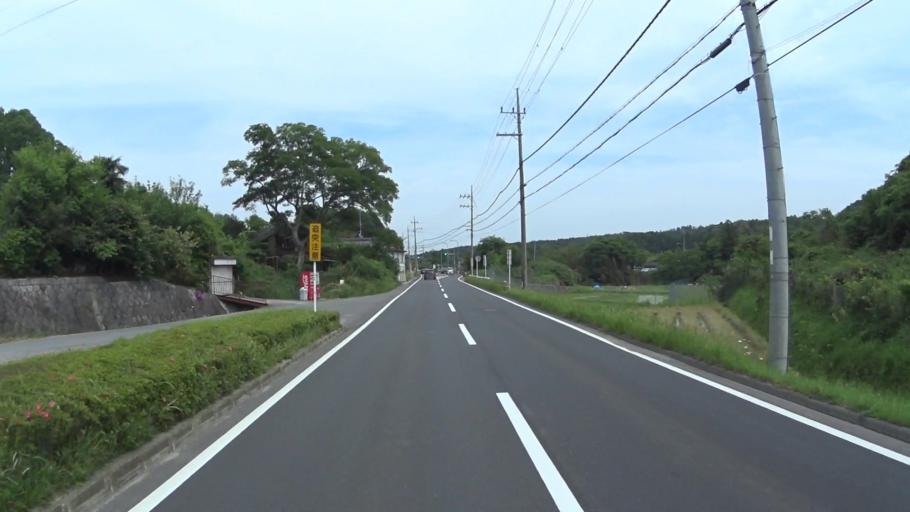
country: JP
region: Shiga Prefecture
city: Kitahama
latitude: 35.1336
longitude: 135.8898
